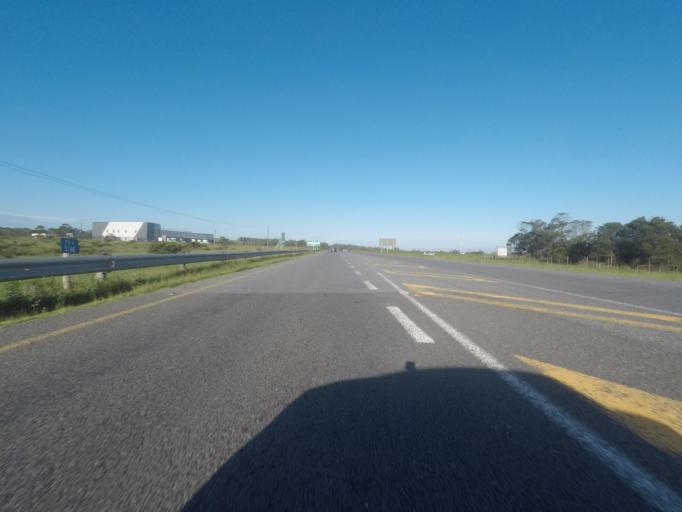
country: ZA
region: Eastern Cape
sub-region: Buffalo City Metropolitan Municipality
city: East London
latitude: -33.0529
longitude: 27.8078
